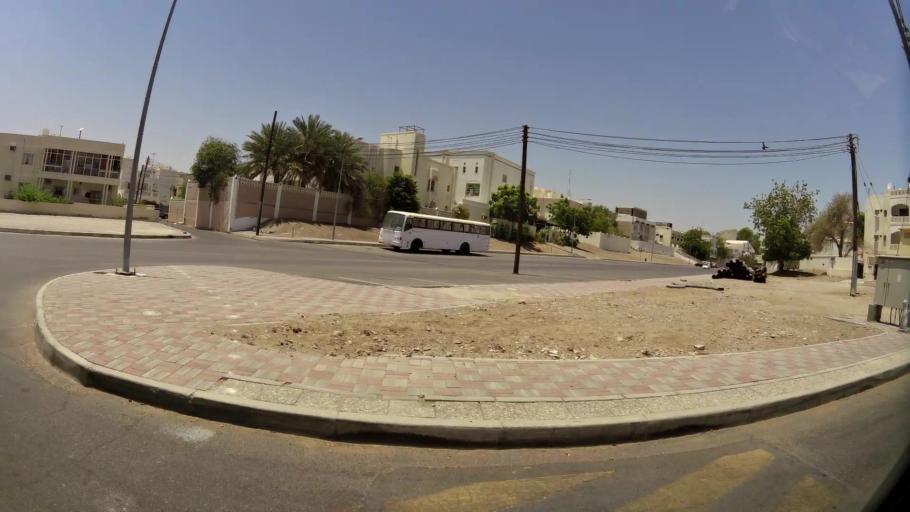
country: OM
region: Muhafazat Masqat
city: Muscat
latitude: 23.6076
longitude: 58.5433
